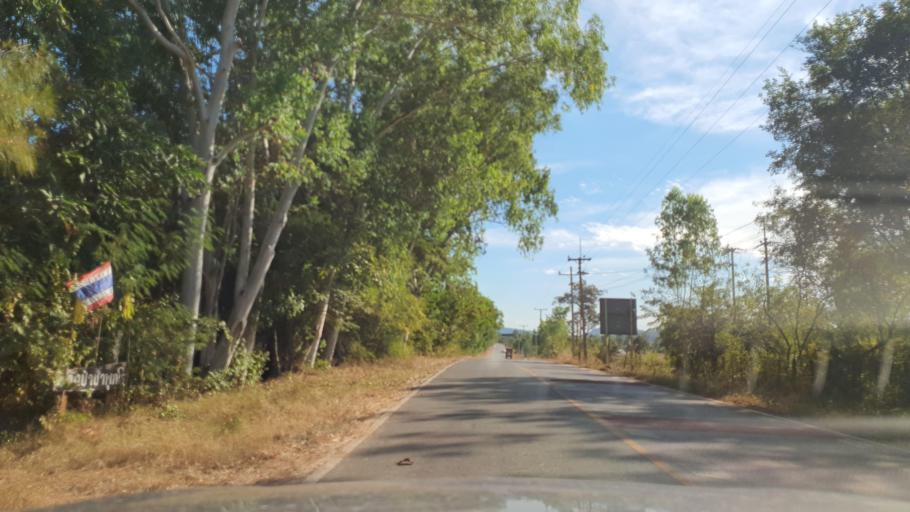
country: TH
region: Kalasin
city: Khao Wong
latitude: 16.6323
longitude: 104.1347
